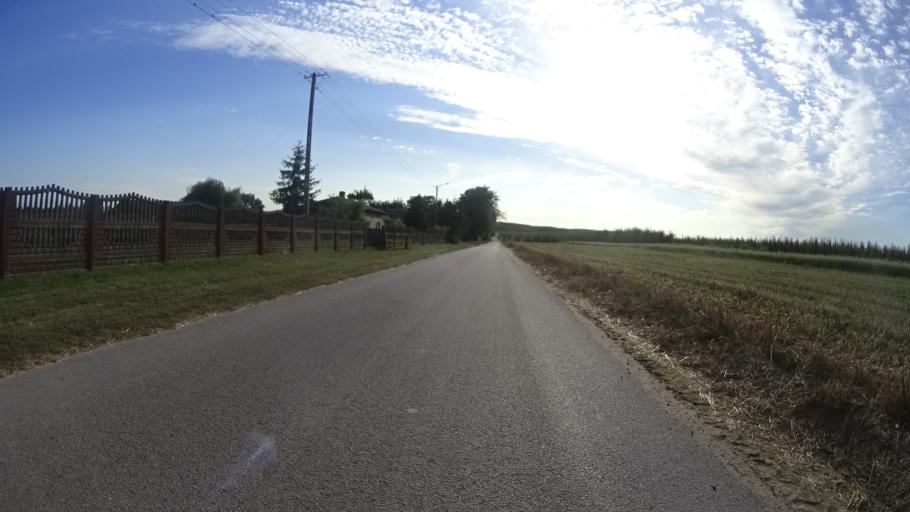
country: PL
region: Masovian Voivodeship
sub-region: Powiat grojecki
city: Goszczyn
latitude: 51.6924
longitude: 20.8103
